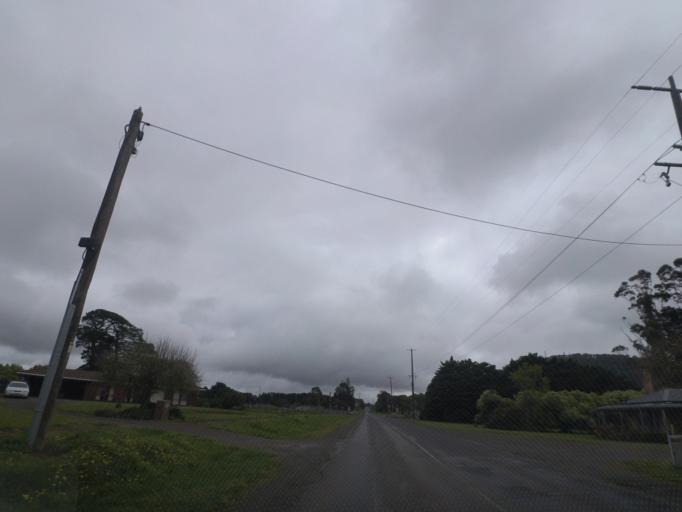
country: AU
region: Victoria
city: Brown Hill
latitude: -37.5892
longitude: 143.9640
